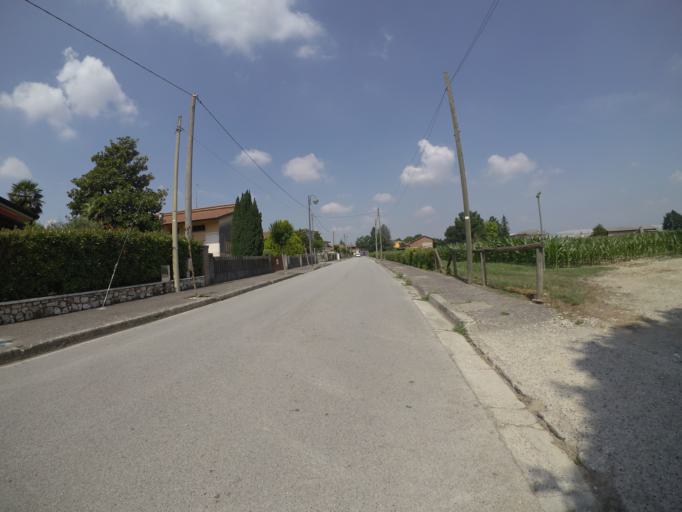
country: IT
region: Friuli Venezia Giulia
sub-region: Provincia di Udine
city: Rivignano
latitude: 45.8839
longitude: 13.0595
